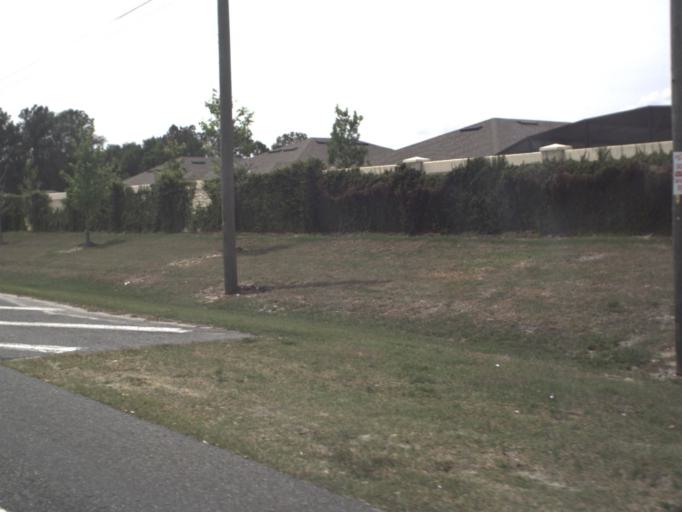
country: US
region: Florida
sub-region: Lake County
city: Mount Dora
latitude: 28.8501
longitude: -81.6339
